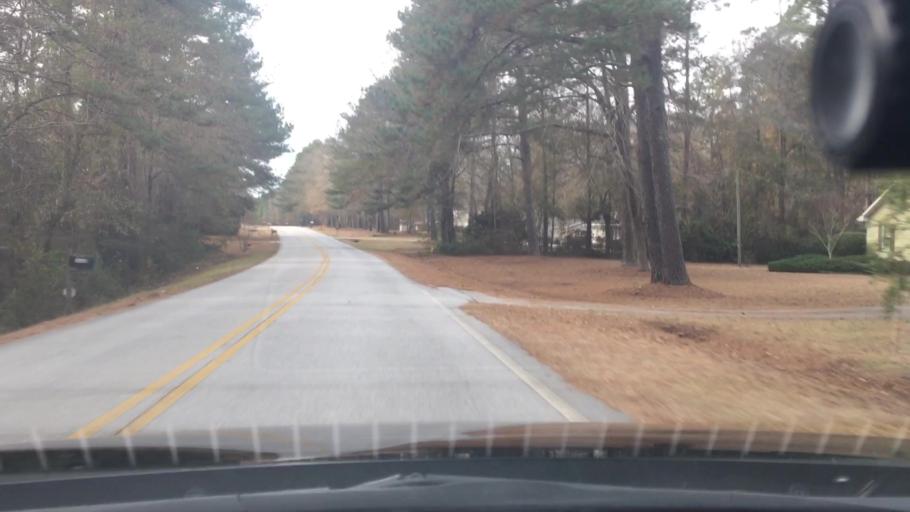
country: US
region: Georgia
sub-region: Spalding County
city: Experiment
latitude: 33.2763
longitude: -84.3218
